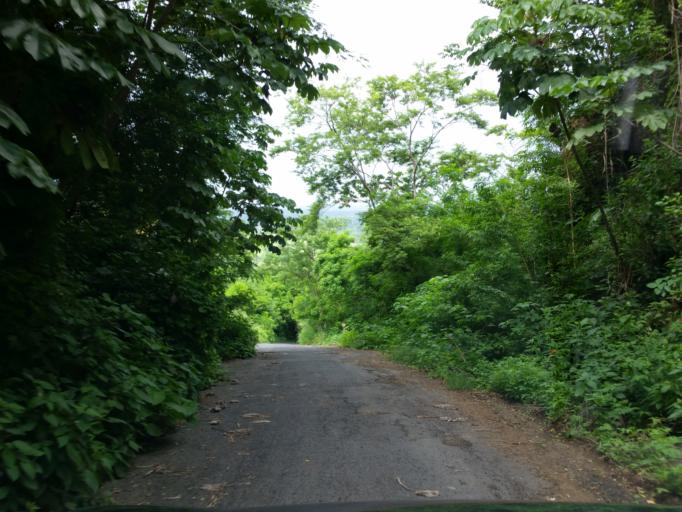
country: NI
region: Masaya
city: Ticuantepe
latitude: 12.0551
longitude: -86.2439
